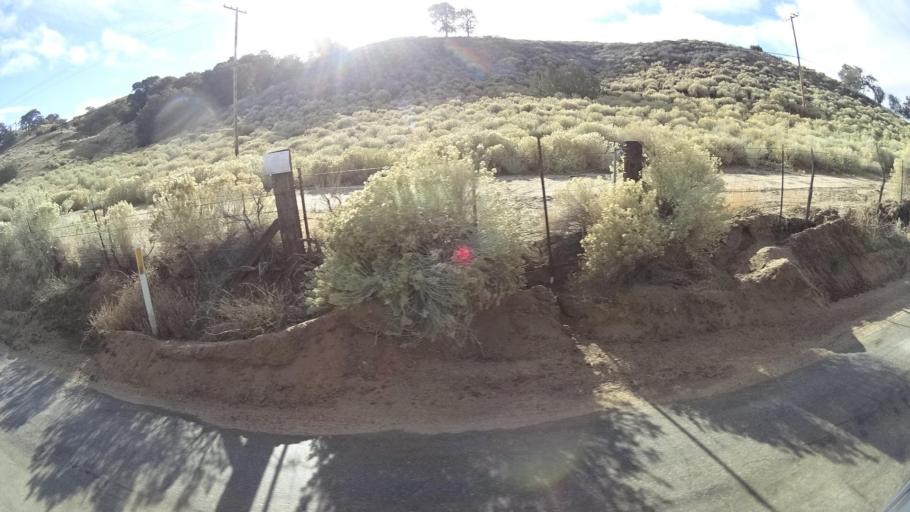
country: US
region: California
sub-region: Kern County
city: Tehachapi
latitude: 35.0768
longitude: -118.3383
